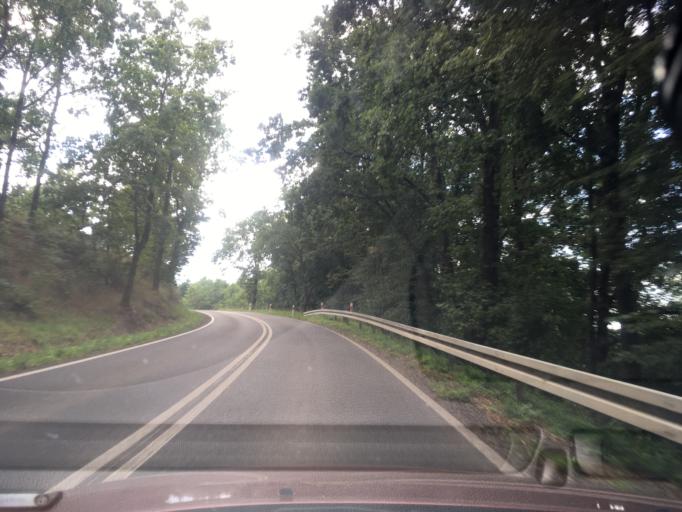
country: PL
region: Lower Silesian Voivodeship
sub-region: Powiat zgorzelecki
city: Zgorzelec
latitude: 51.1950
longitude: 15.0139
